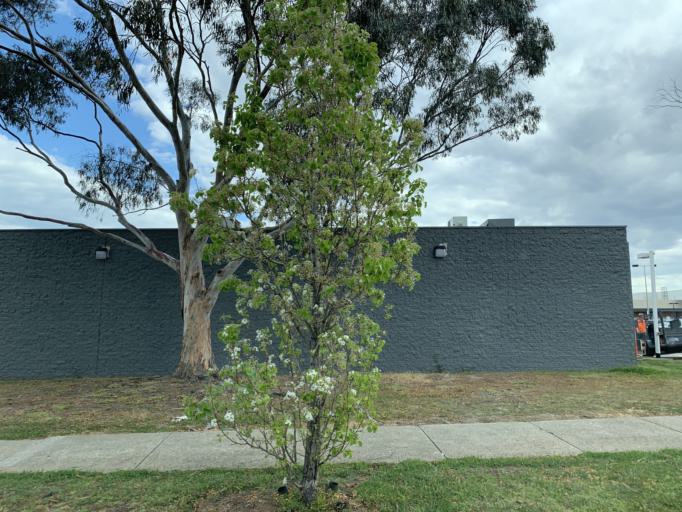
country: AU
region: Victoria
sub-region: Moonee Valley
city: Keilor East
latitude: -37.7484
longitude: 144.8620
